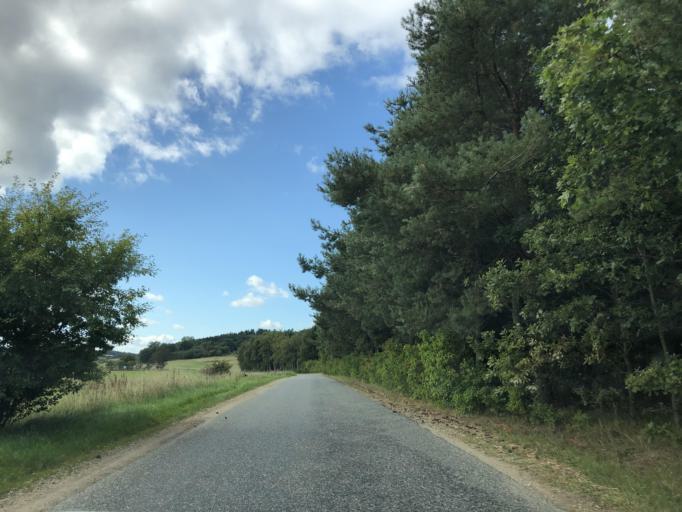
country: DK
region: Central Jutland
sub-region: Viborg Kommune
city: Viborg
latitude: 56.5747
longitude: 9.3474
